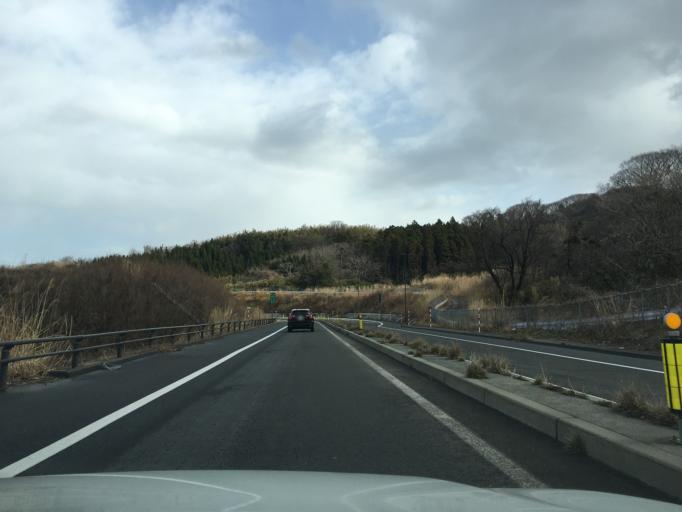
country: JP
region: Yamagata
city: Yuza
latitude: 39.2934
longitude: 139.9768
